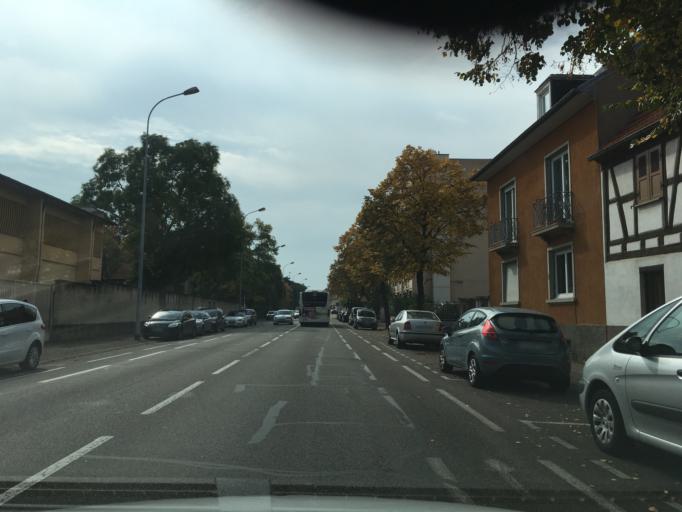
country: FR
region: Alsace
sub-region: Departement du Haut-Rhin
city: Colmar
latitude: 48.0832
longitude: 7.3656
